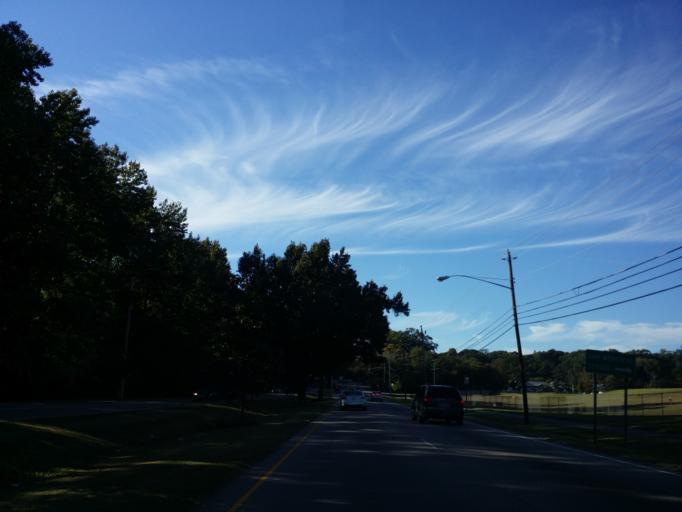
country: US
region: North Carolina
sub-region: Wake County
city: West Raleigh
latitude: 35.7766
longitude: -78.6608
